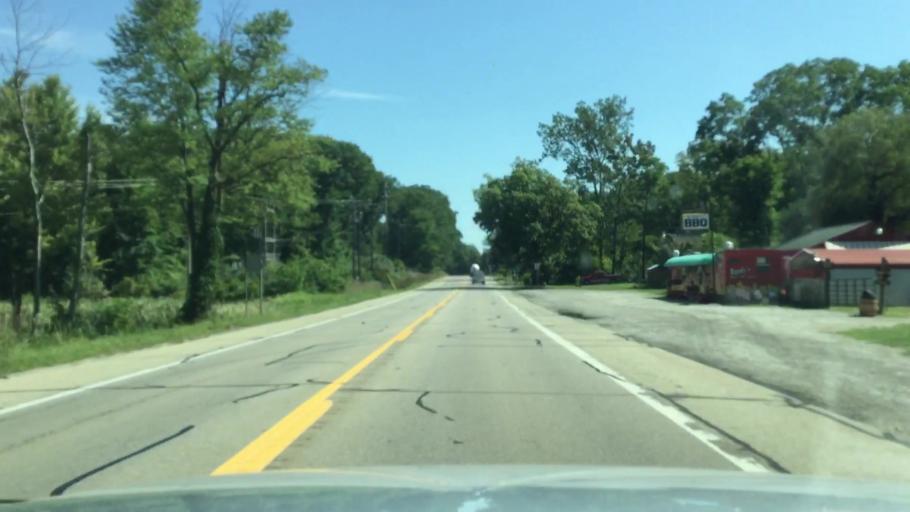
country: US
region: Michigan
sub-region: Jackson County
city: Brooklyn
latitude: 42.0592
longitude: -84.1318
